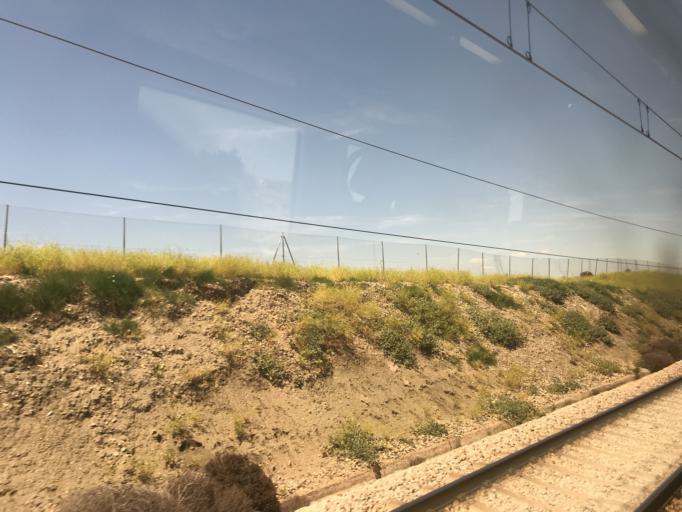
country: ES
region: Madrid
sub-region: Provincia de Madrid
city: Villaverde
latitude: 40.3273
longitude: -3.7071
